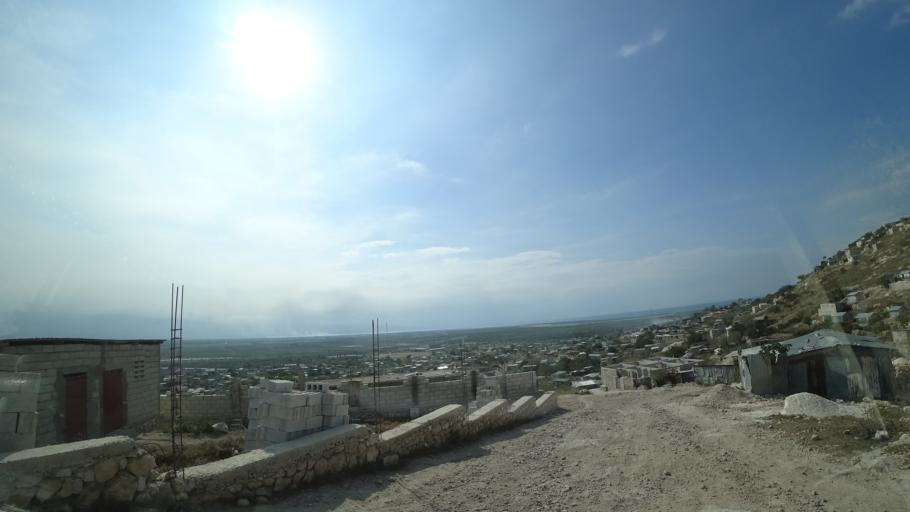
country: HT
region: Ouest
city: Croix des Bouquets
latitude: 18.6602
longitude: -72.2820
